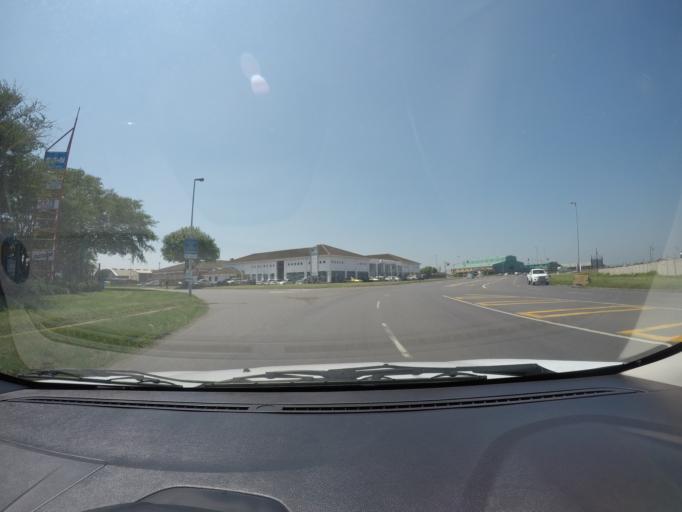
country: ZA
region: KwaZulu-Natal
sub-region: uThungulu District Municipality
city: Richards Bay
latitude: -28.7549
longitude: 32.0254
